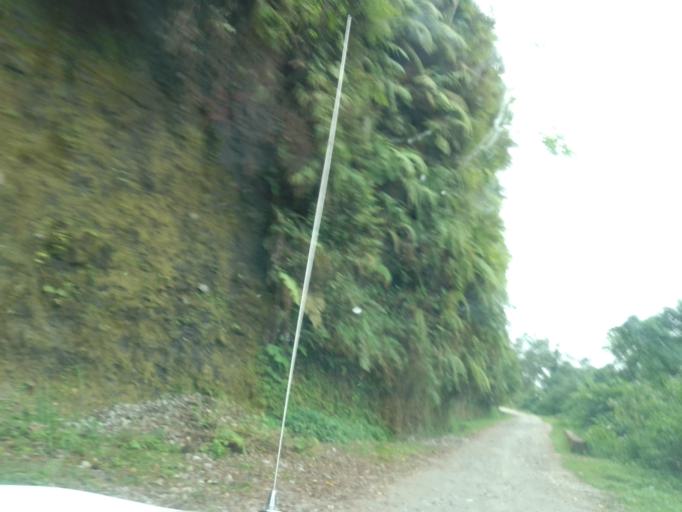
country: MX
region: Chiapas
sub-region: Union Juarez
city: Santo Domingo
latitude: 15.0931
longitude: -92.0919
